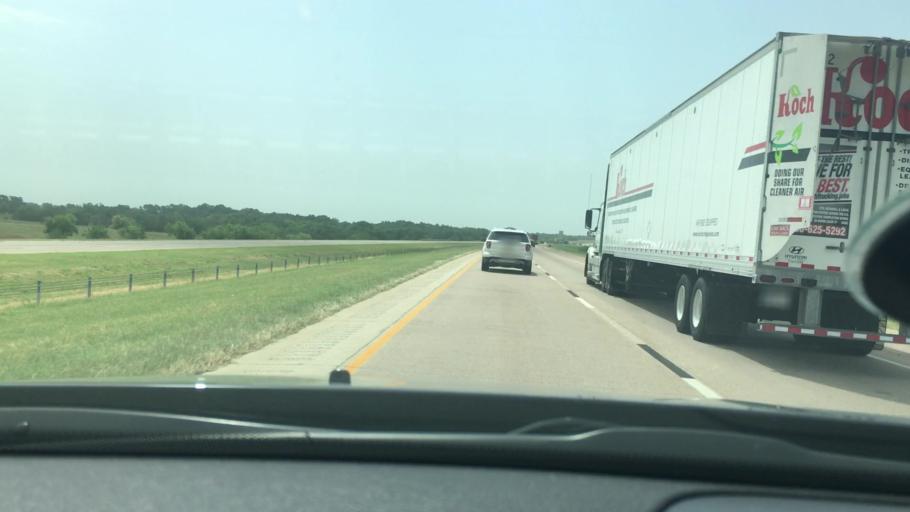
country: US
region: Oklahoma
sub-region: Garvin County
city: Pauls Valley
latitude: 34.6993
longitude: -97.2392
